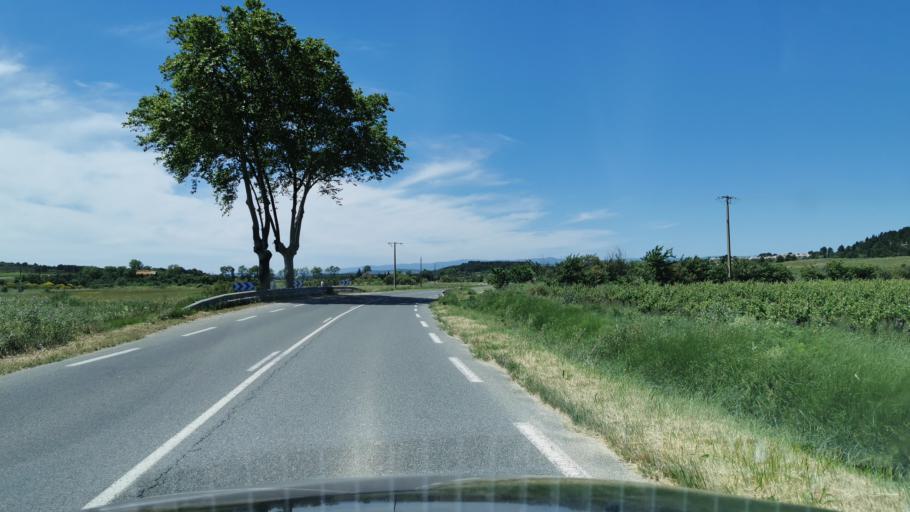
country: FR
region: Languedoc-Roussillon
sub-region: Departement de l'Aude
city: Marcorignan
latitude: 43.2128
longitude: 2.9367
